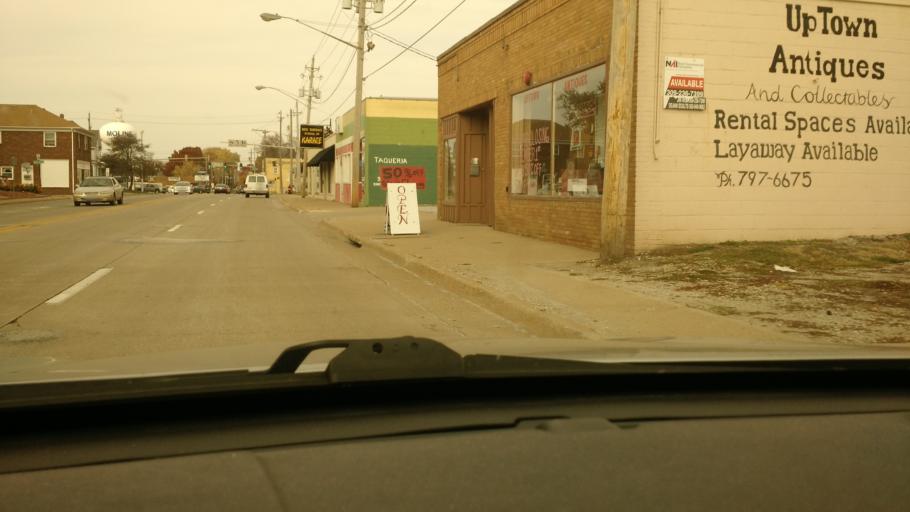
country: US
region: Illinois
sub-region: Rock Island County
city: Moline
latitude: 41.4916
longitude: -90.5135
